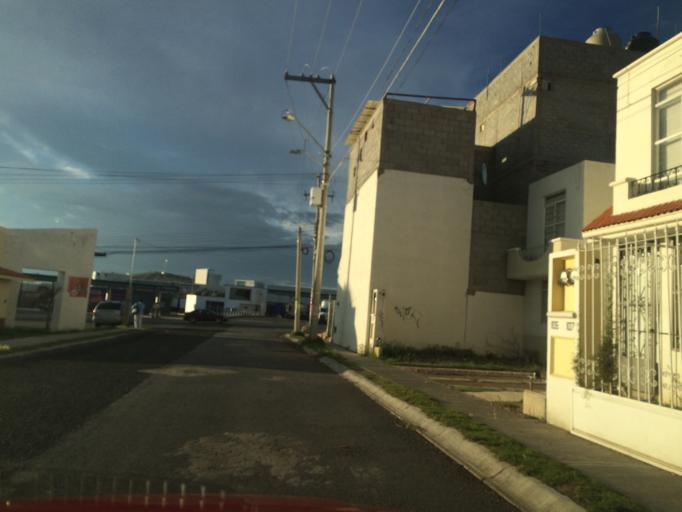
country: MX
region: Zacatecas
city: Zacatecas
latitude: 22.7693
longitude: -102.6116
